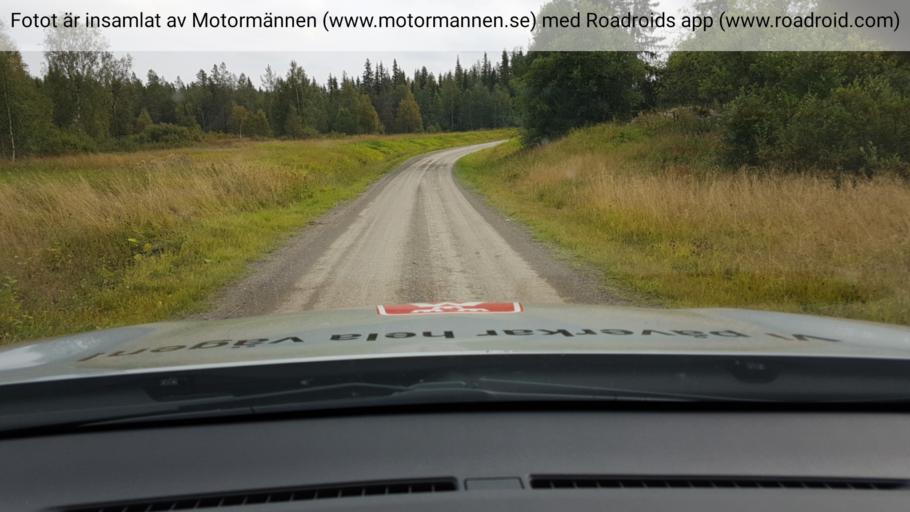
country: SE
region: Jaemtland
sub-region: Stroemsunds Kommun
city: Stroemsund
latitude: 63.7637
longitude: 15.3468
